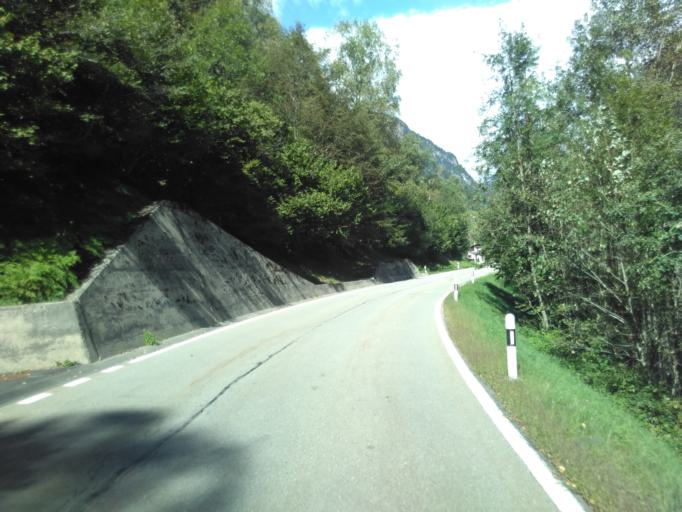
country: CH
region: Grisons
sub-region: Moesa District
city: Cauco
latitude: 46.3270
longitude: 9.1181
